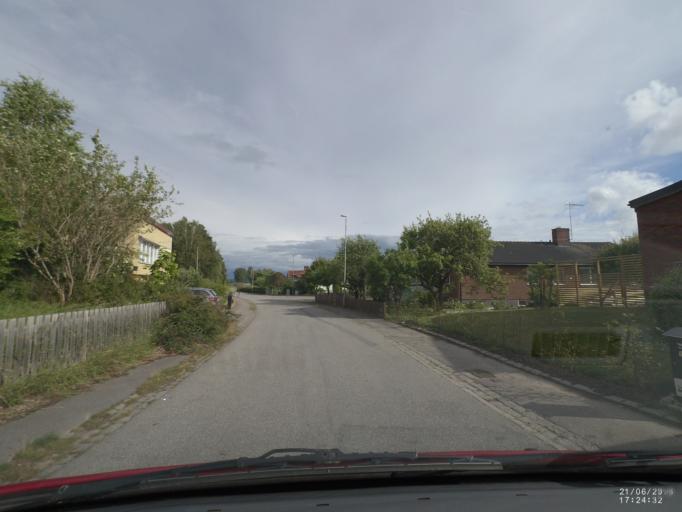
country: SE
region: Soedermanland
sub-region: Nykopings Kommun
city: Nykoping
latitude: 58.7523
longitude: 17.0528
